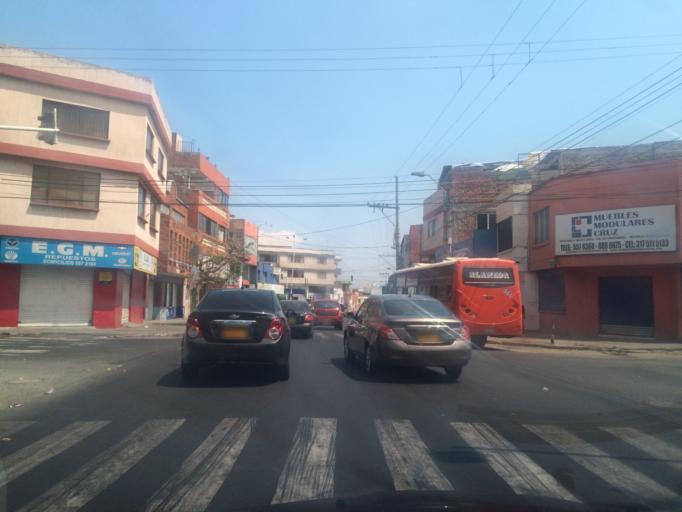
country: CO
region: Valle del Cauca
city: Cali
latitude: 3.4425
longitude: -76.5343
